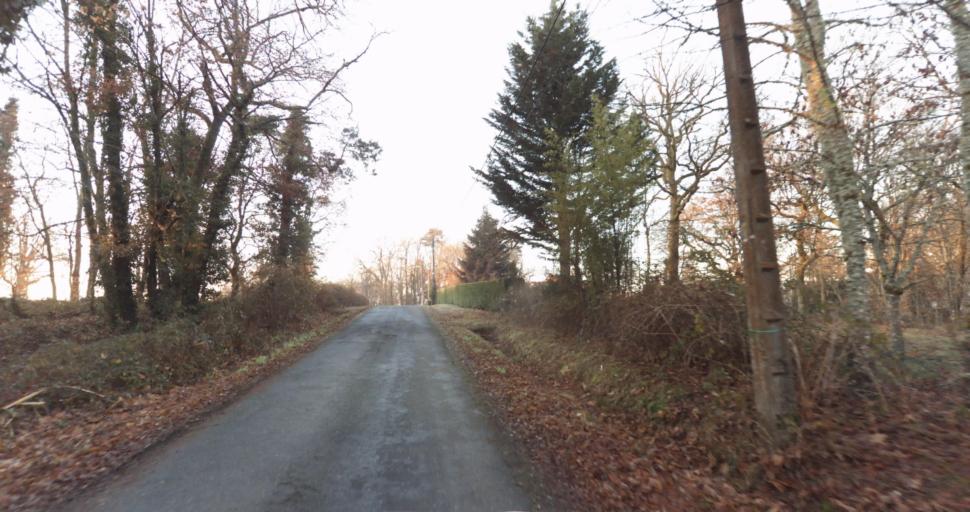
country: FR
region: Limousin
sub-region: Departement de la Haute-Vienne
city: Aixe-sur-Vienne
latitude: 45.8158
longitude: 1.1610
